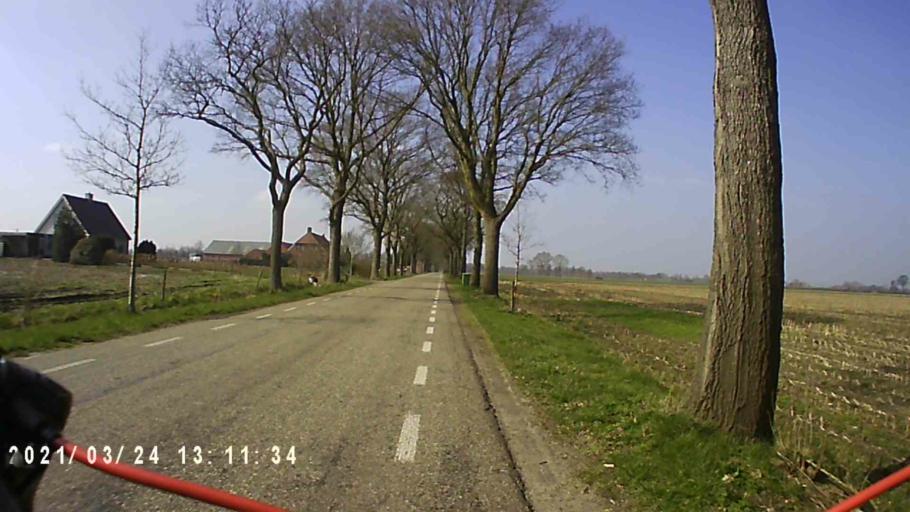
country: NL
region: Groningen
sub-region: Gemeente Leek
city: Leek
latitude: 53.1206
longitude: 6.3015
